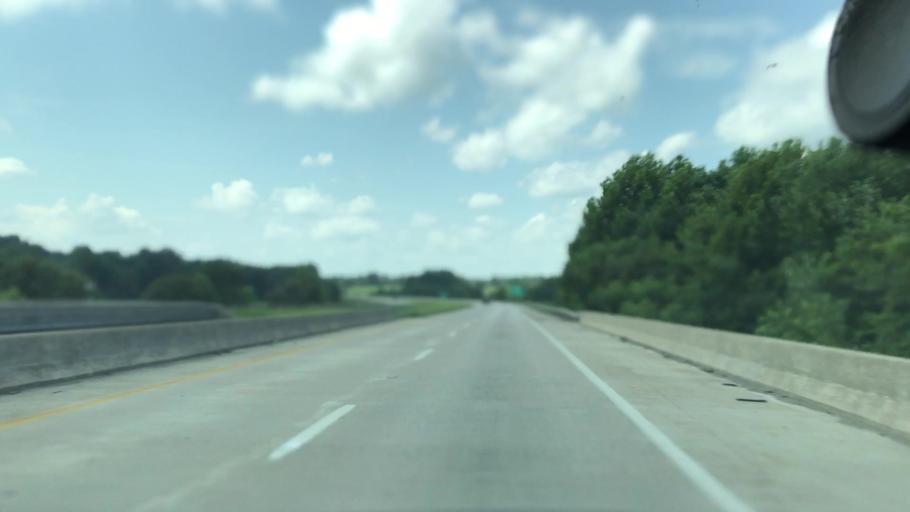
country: US
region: Ohio
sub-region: Gallia County
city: Gallipolis
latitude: 38.8918
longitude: -82.3581
